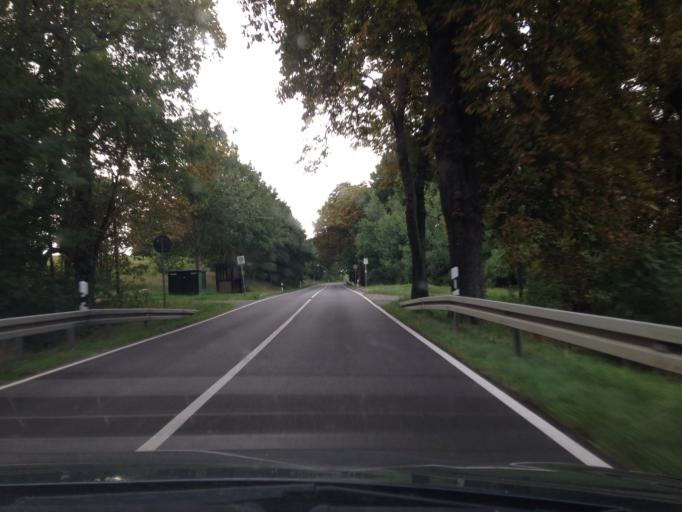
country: DE
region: Mecklenburg-Vorpommern
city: Loitz
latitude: 53.3538
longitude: 13.4070
